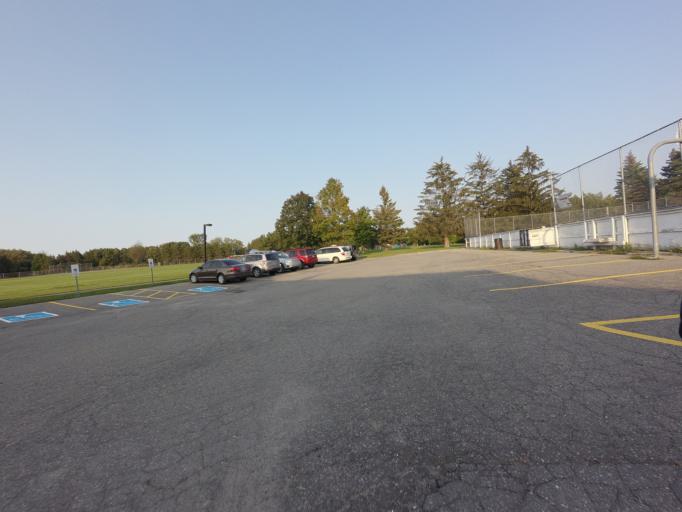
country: CA
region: Ontario
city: Bells Corners
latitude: 45.2897
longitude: -75.8789
